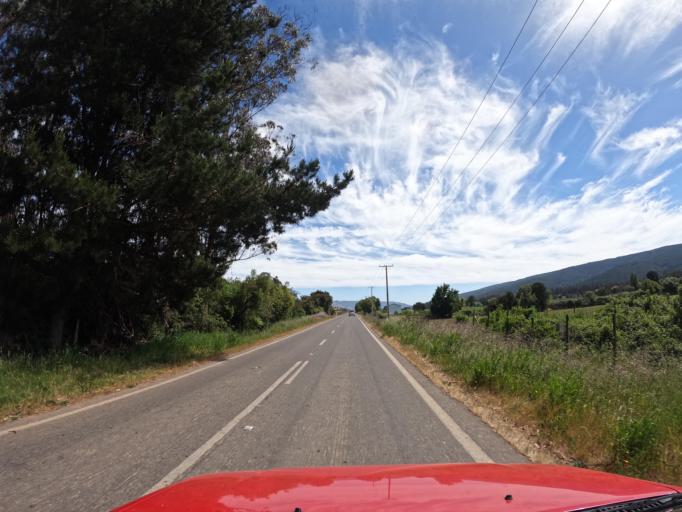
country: CL
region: Maule
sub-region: Provincia de Talca
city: Constitucion
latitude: -34.9953
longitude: -72.0200
